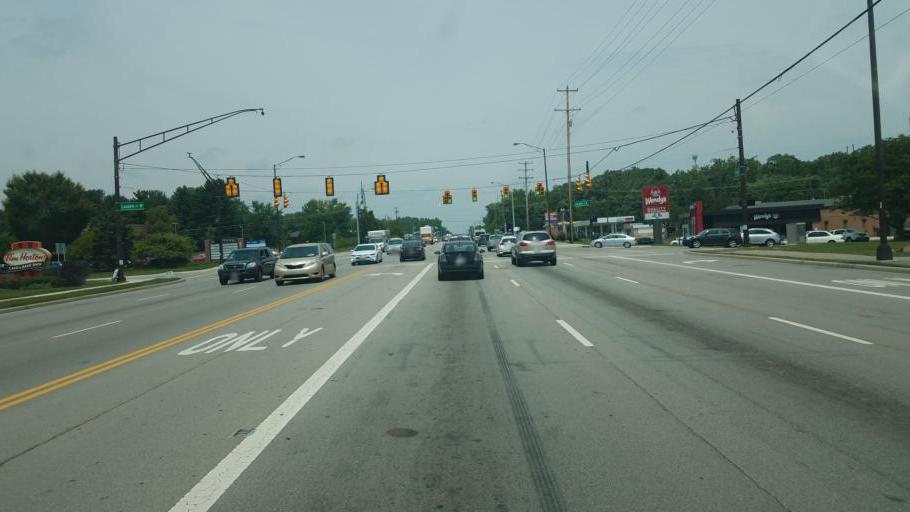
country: US
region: Ohio
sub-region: Franklin County
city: Worthington
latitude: 40.1351
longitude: -83.0168
